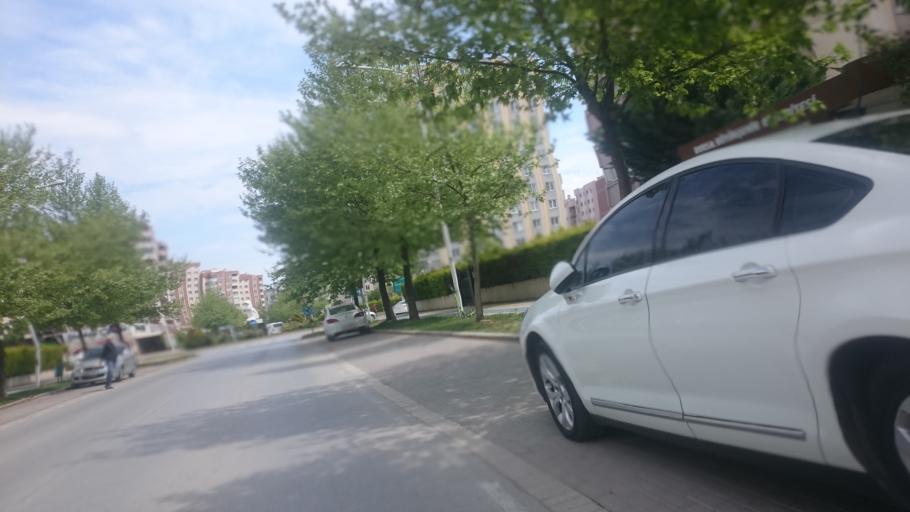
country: TR
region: Bursa
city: Cali
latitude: 40.2262
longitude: 28.9078
